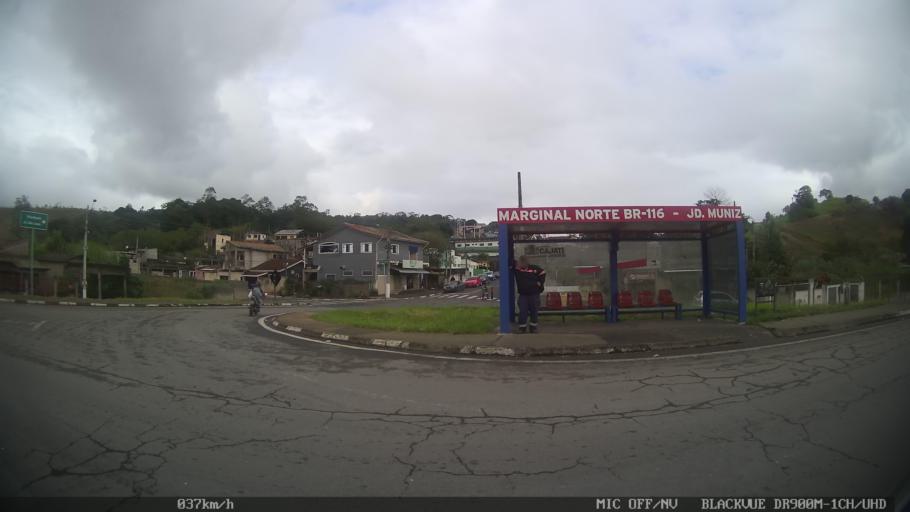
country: BR
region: Sao Paulo
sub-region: Cajati
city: Cajati
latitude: -24.7316
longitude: -48.0979
